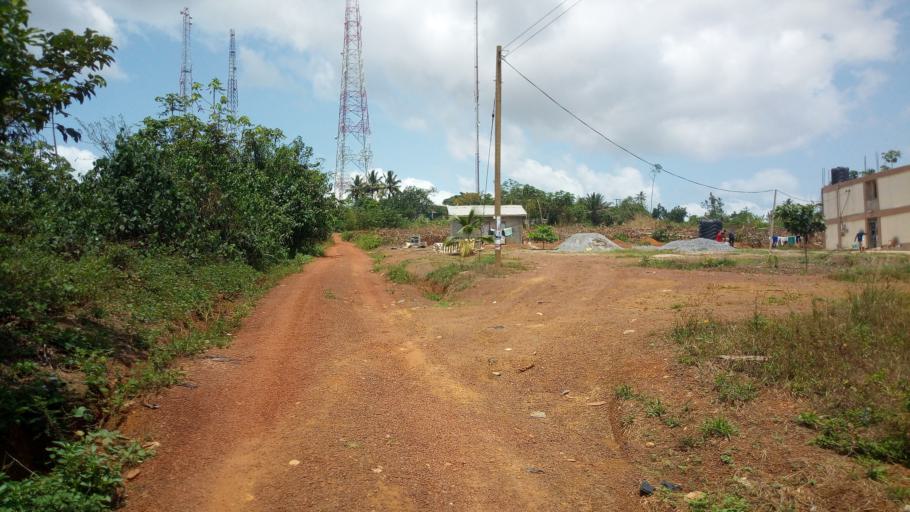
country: GH
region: Western
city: Tarkwa
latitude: 5.3016
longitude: -2.0056
